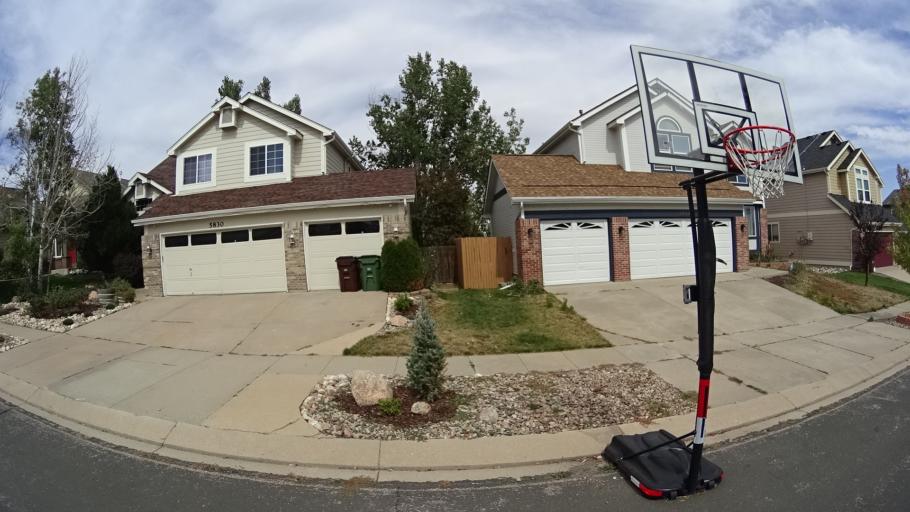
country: US
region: Colorado
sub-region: El Paso County
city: Cimarron Hills
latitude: 38.9016
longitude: -104.7073
